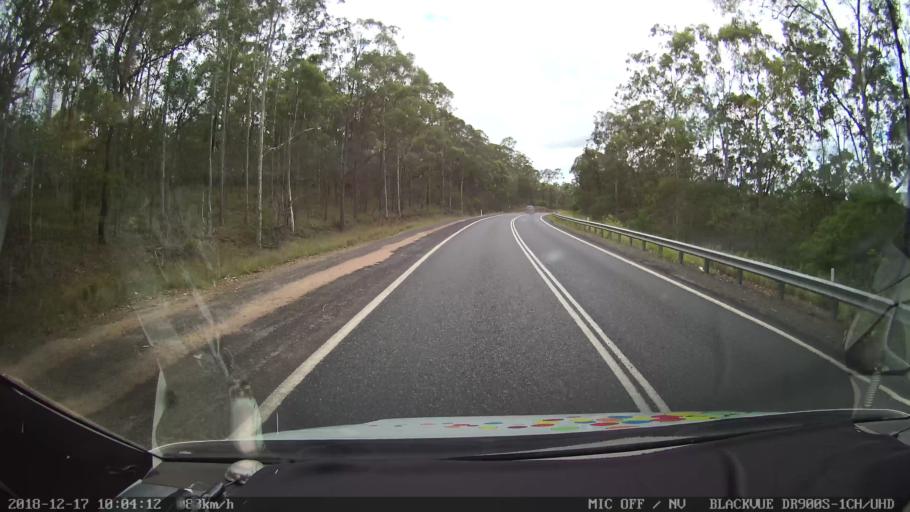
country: AU
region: New South Wales
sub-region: Tenterfield Municipality
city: Carrolls Creek
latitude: -28.8940
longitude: 152.4740
